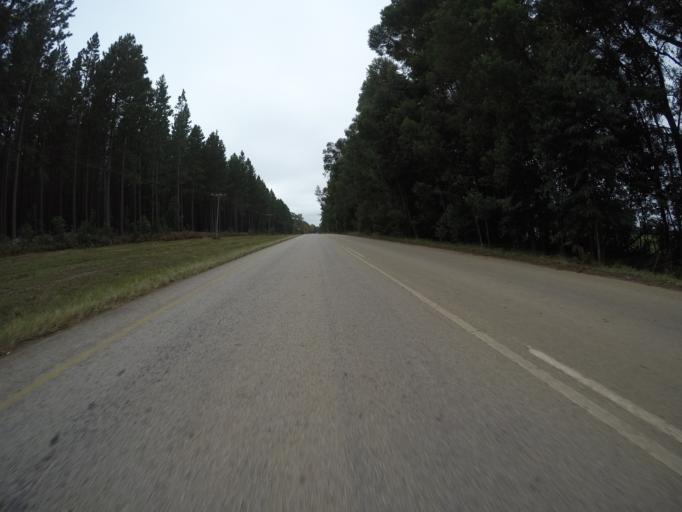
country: ZA
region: Eastern Cape
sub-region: Cacadu District Municipality
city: Kareedouw
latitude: -33.9943
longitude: 24.1124
